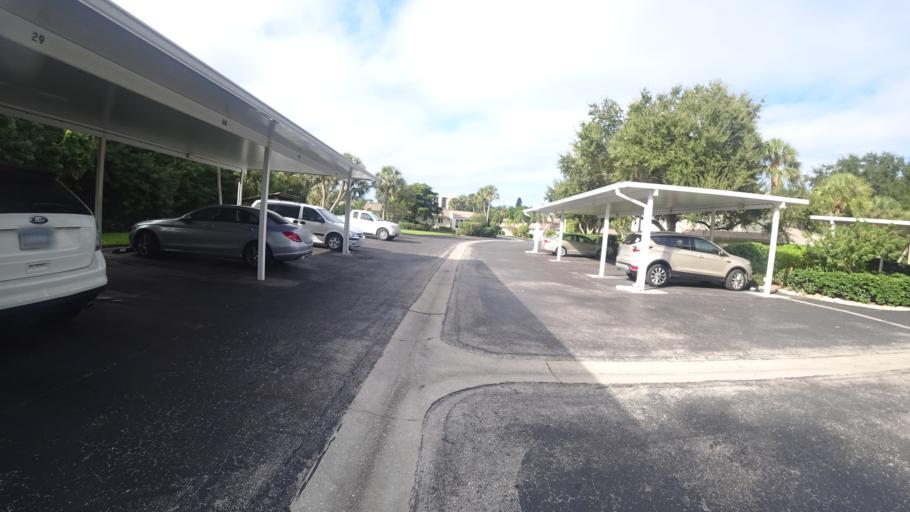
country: US
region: Florida
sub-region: Manatee County
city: Longboat Key
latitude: 27.3945
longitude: -82.6410
